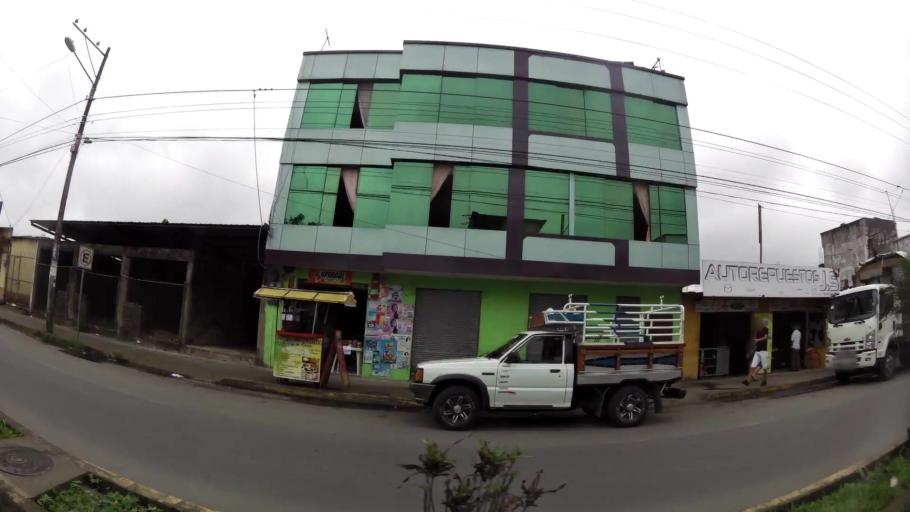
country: EC
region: Santo Domingo de los Tsachilas
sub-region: Canton Santo Domingo de los Colorados
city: Santo Domingo de los Colorados
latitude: -0.2548
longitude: -79.1976
